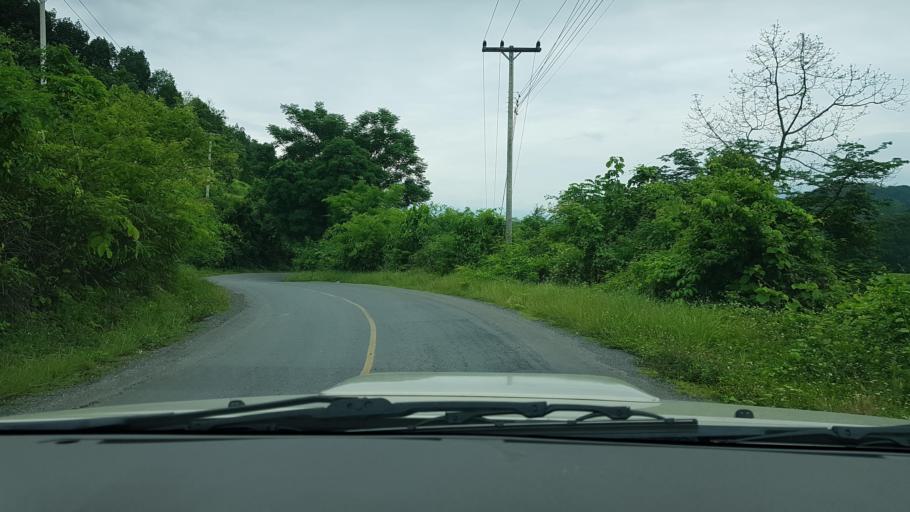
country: LA
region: Loungnamtha
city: Muang Nale
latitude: 20.1659
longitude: 101.5085
